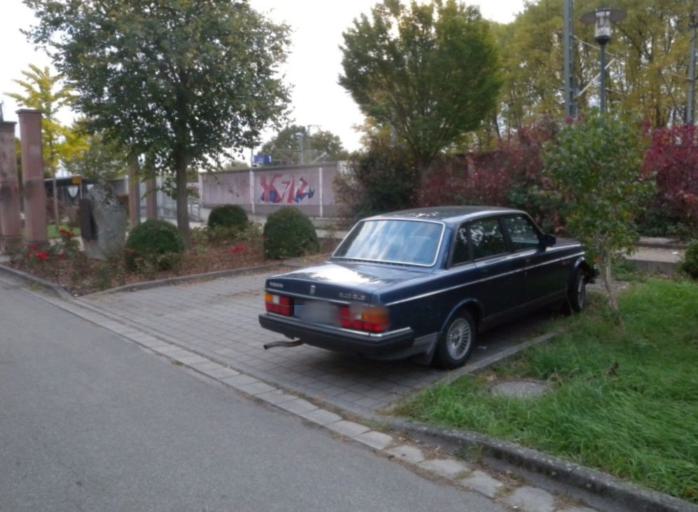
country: DE
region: Baden-Wuerttemberg
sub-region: Freiburg Region
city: Appenweier
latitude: 48.5429
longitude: 7.9742
